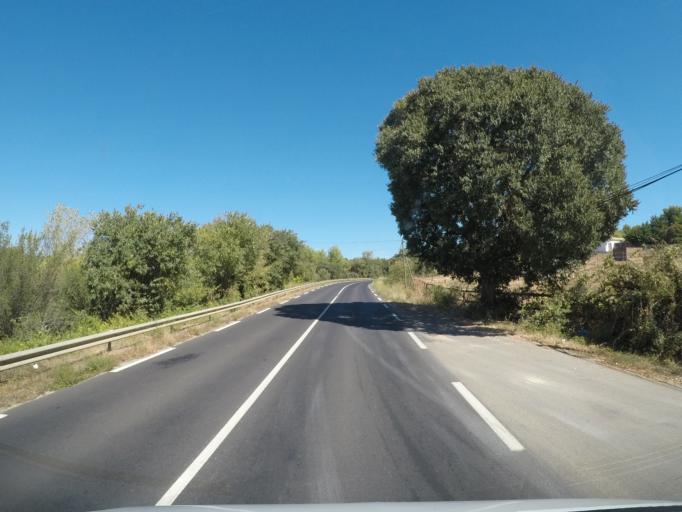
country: FR
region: Languedoc-Roussillon
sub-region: Departement de l'Herault
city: Aniane
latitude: 43.7024
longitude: 3.5943
